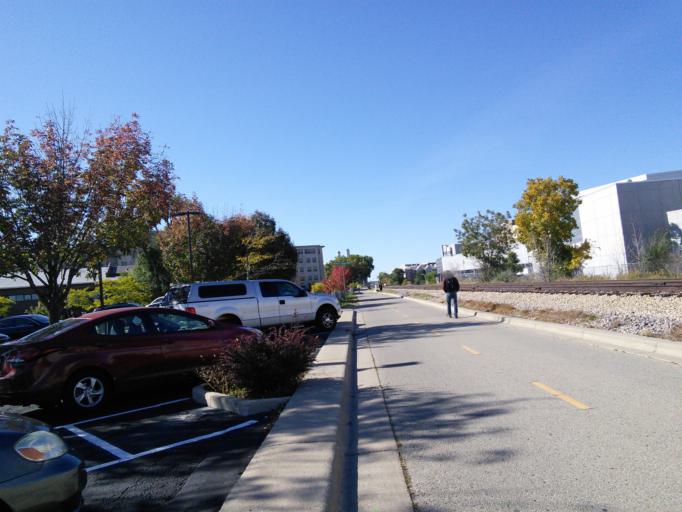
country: US
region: Wisconsin
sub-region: Dane County
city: Madison
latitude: 43.0688
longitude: -89.3979
